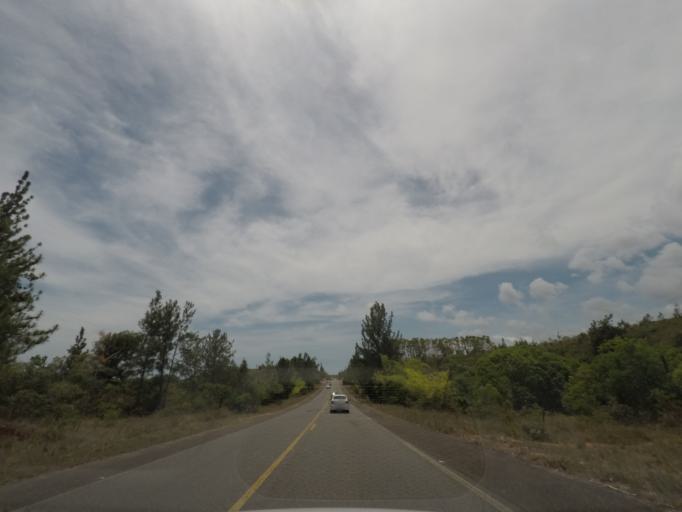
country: BR
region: Bahia
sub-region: Conde
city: Conde
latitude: -12.0052
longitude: -37.6852
